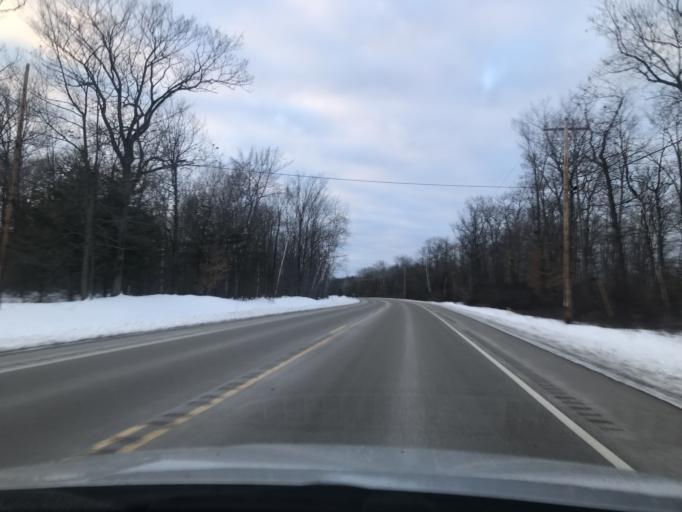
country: US
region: Wisconsin
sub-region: Marinette County
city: Marinette
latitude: 45.1520
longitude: -87.7061
